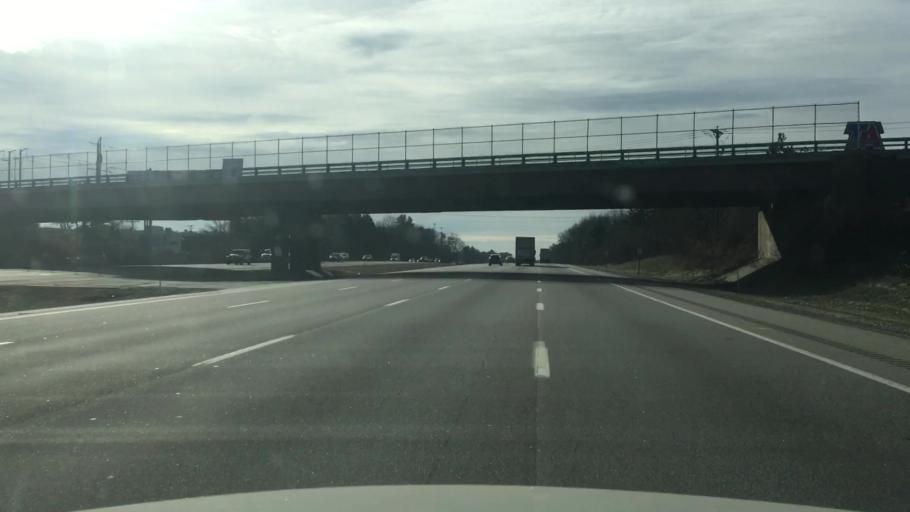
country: US
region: New Hampshire
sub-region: Rockingham County
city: Greenland
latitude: 43.0430
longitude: -70.8166
